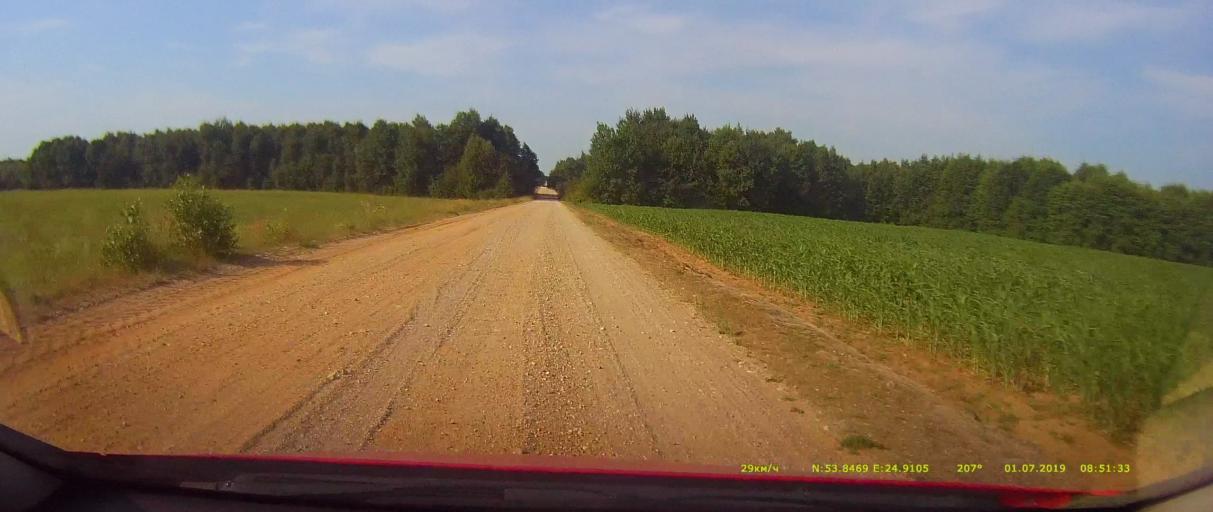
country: BY
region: Grodnenskaya
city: Shchuchin
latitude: 53.8469
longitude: 24.9104
